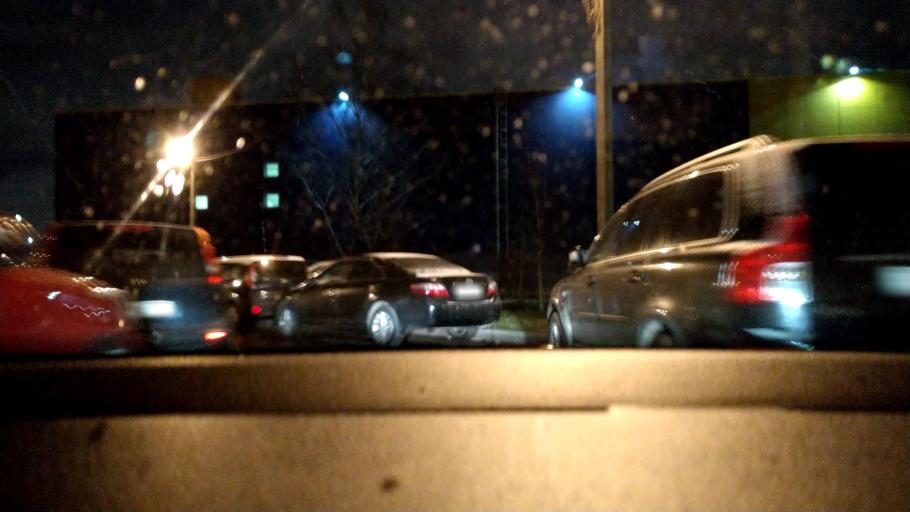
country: RU
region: Moscow
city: Strogino
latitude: 55.8615
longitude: 37.3939
